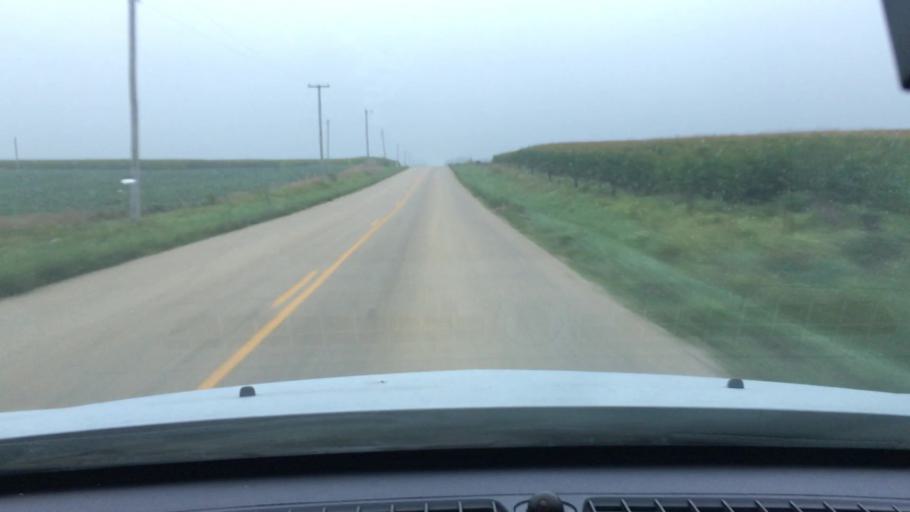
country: US
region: Illinois
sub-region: DeKalb County
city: Malta
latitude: 41.8638
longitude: -88.9614
